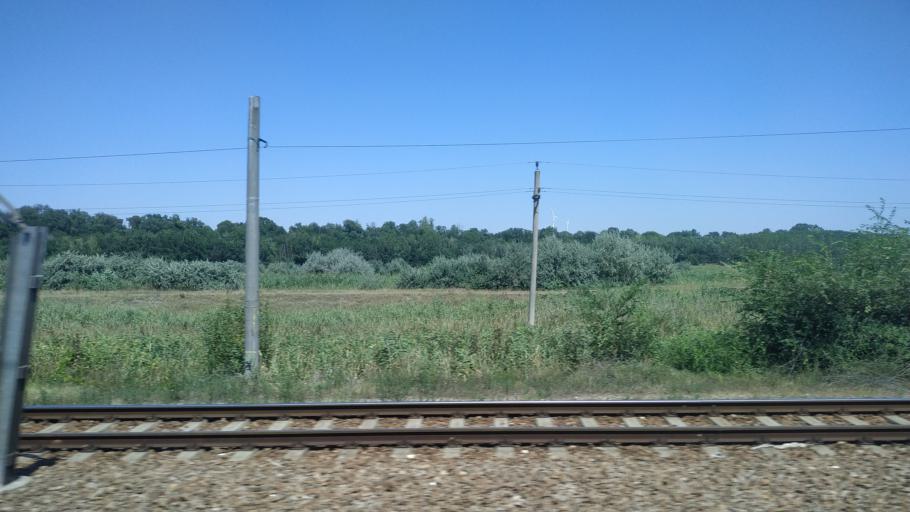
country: RO
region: Constanta
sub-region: Comuna Mircea Voda
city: Mircea Voda
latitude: 44.2652
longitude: 28.1515
